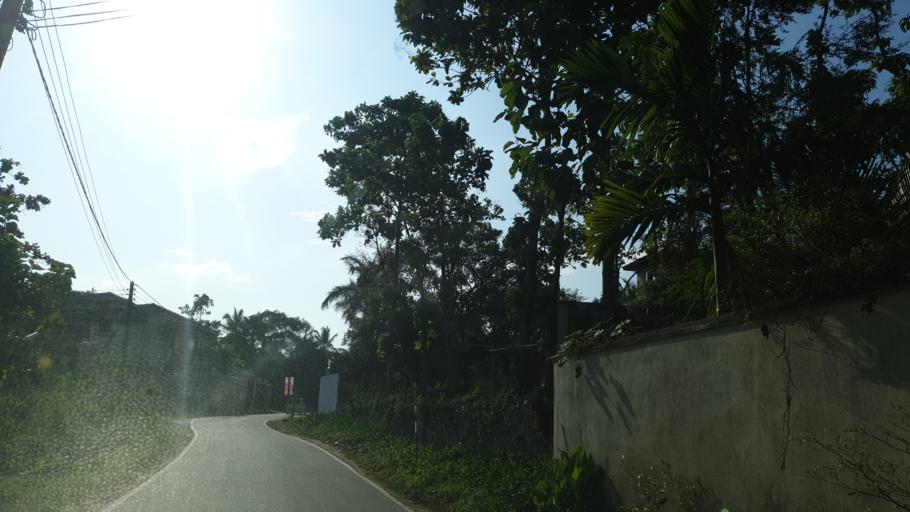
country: LK
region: Western
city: Battaramulla South
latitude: 6.8895
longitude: 79.9458
